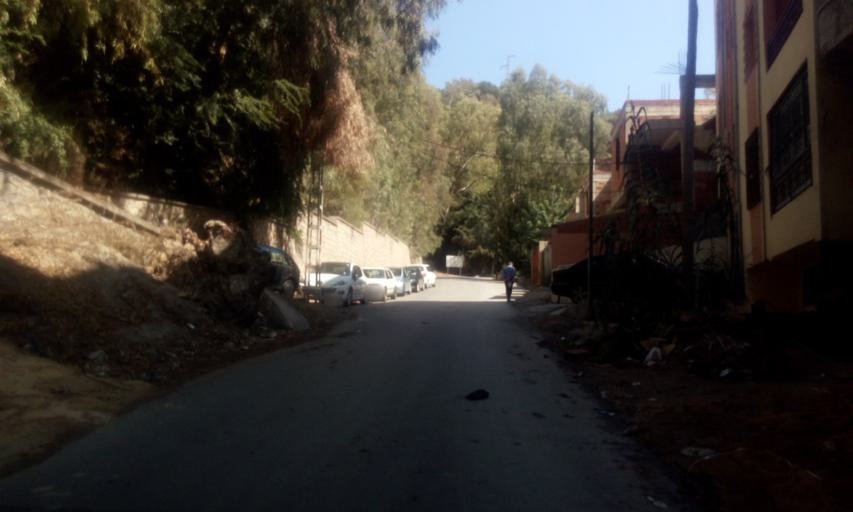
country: DZ
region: Bejaia
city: Bejaia
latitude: 36.7614
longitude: 5.0858
